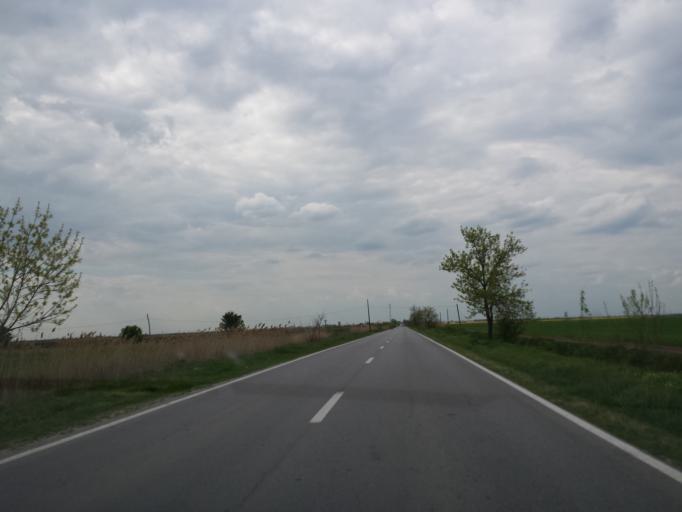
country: RO
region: Timis
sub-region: Comuna Sanpetru Mare
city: Sanpetru Mare
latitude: 46.0349
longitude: 20.6577
